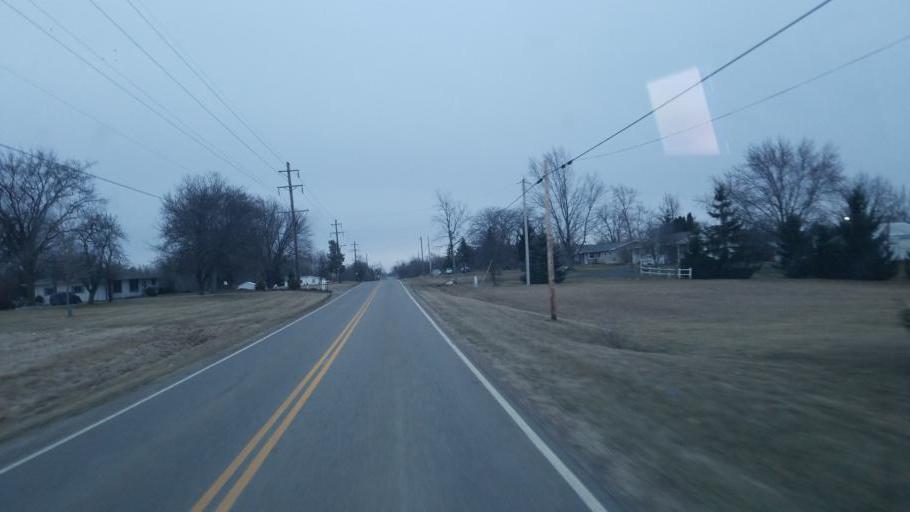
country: US
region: Ohio
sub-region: Defiance County
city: Hicksville
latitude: 41.3227
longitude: -84.7667
